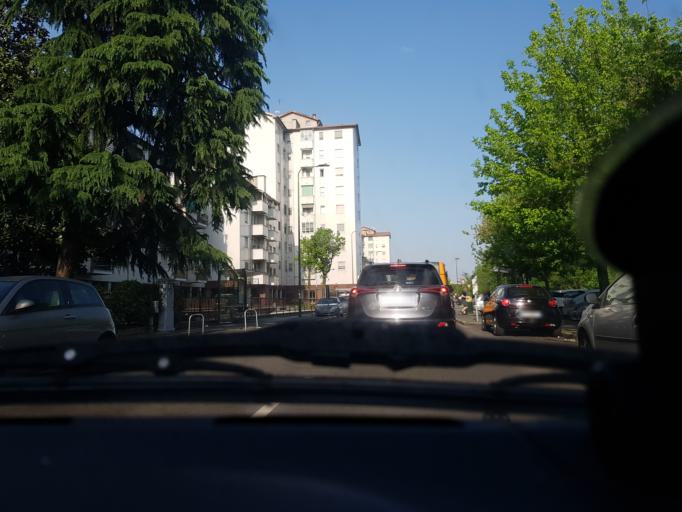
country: IT
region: Lombardy
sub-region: Citta metropolitana di Milano
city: Cesano Boscone
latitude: 45.4555
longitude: 9.1097
